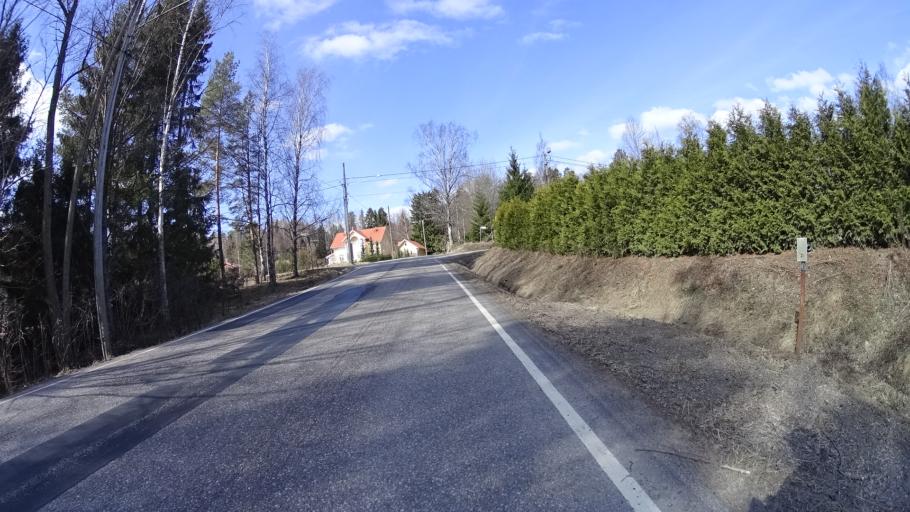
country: FI
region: Uusimaa
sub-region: Helsinki
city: Kauniainen
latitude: 60.2533
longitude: 24.7319
